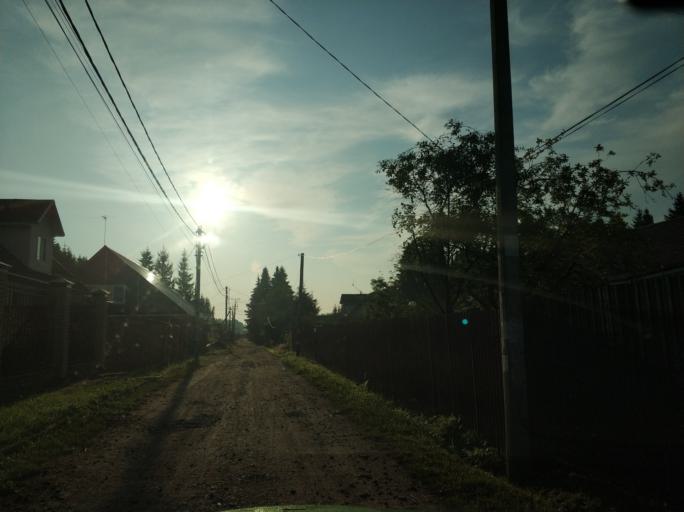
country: RU
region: Leningrad
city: Shcheglovo
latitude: 60.0524
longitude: 30.7507
